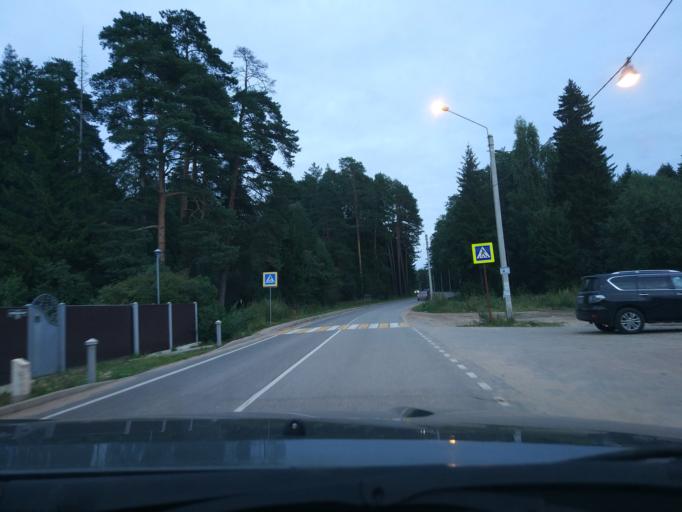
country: RU
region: Tverskaya
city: Konakovo
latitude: 56.6965
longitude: 36.7381
